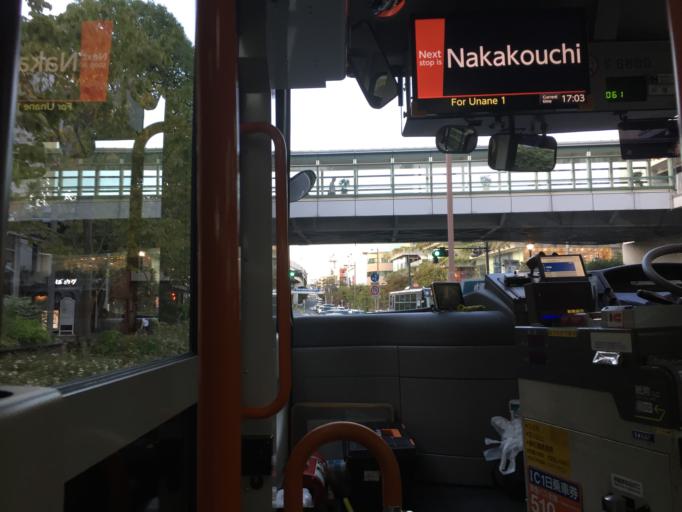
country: JP
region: Tokyo
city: Chofugaoka
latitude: 35.6141
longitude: 139.6273
